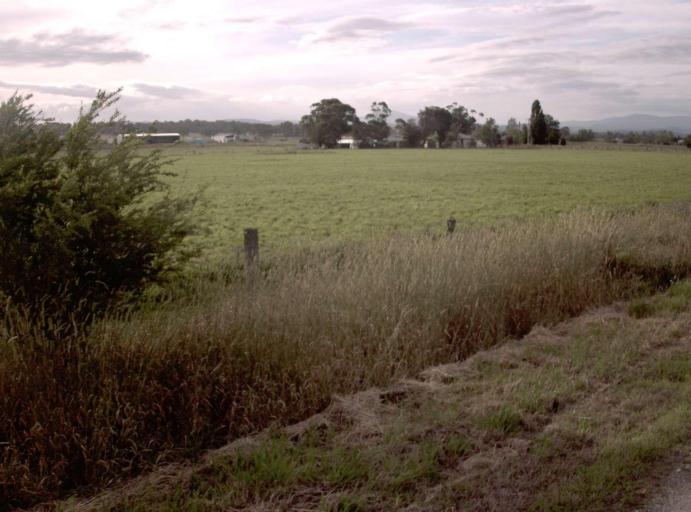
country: AU
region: Victoria
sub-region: Wellington
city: Heyfield
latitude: -37.8967
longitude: 146.9920
